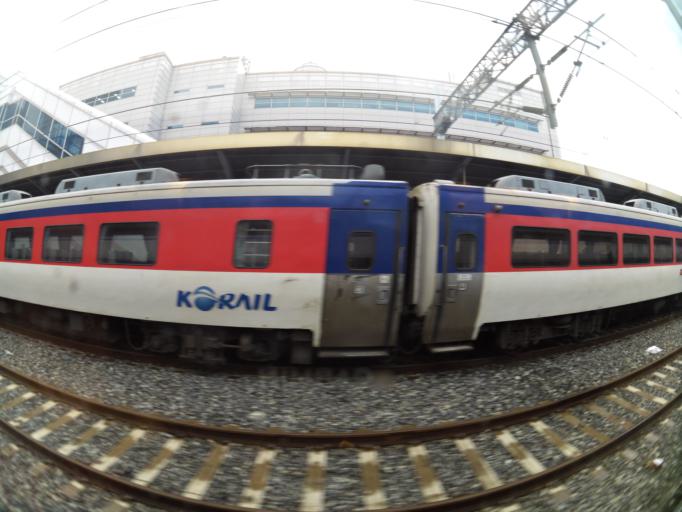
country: KR
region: Daejeon
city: Daejeon
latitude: 36.3327
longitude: 127.4336
